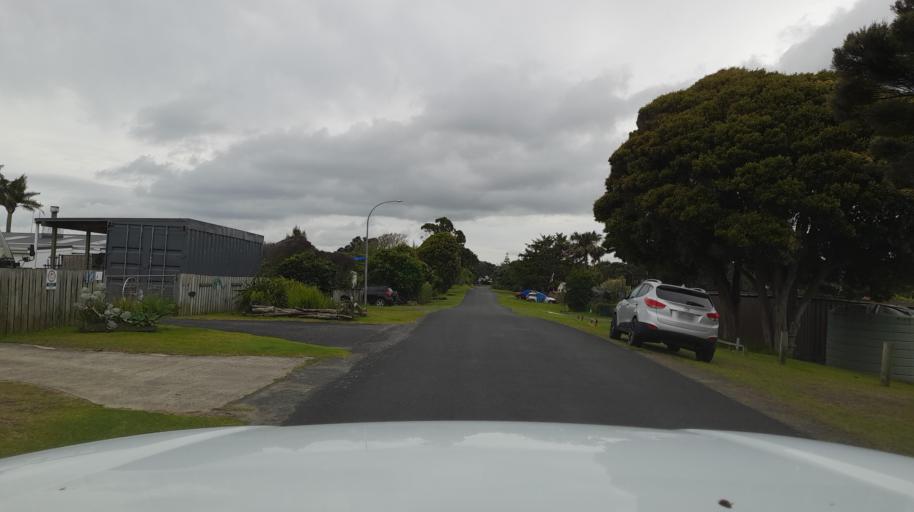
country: NZ
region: Northland
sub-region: Far North District
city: Ahipara
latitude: -35.1633
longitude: 173.1568
